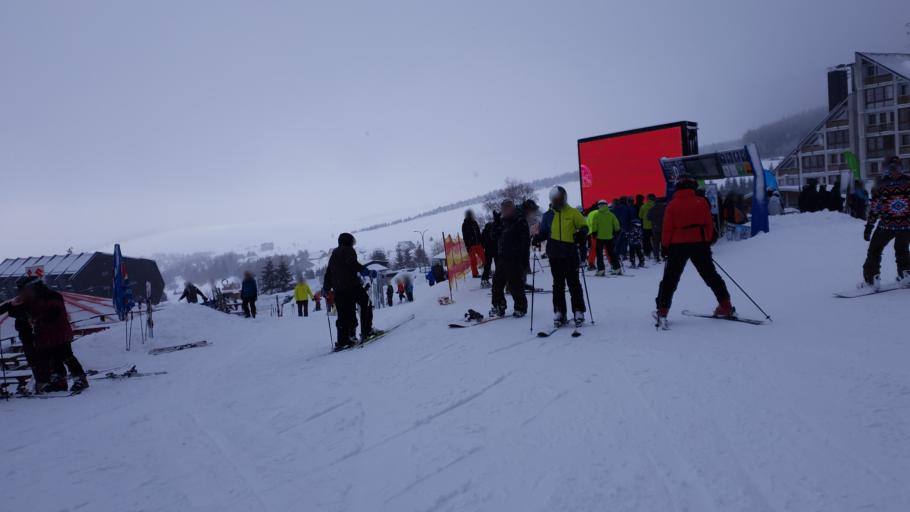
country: DE
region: Saxony
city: Kurort Oberwiesenthal
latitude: 50.4032
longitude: 12.9829
